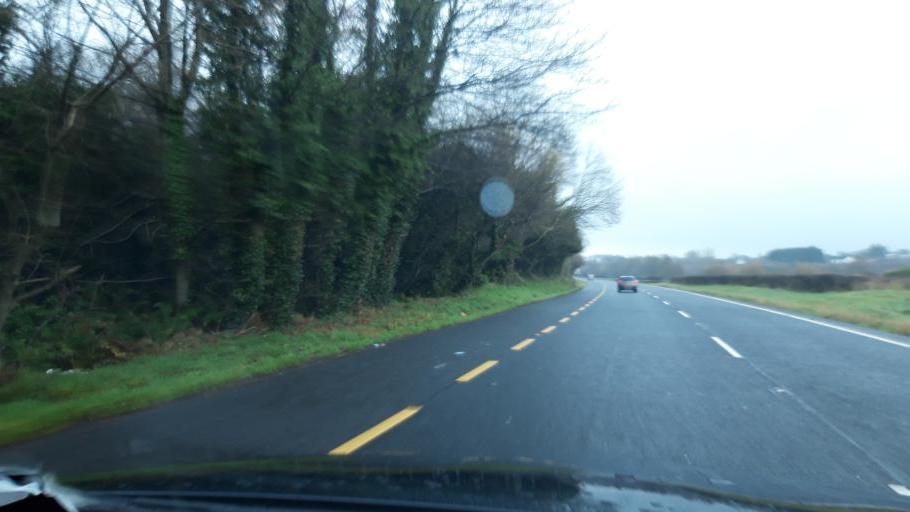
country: IE
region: Ulster
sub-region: County Donegal
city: Letterkenny
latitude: 54.9469
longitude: -7.6737
